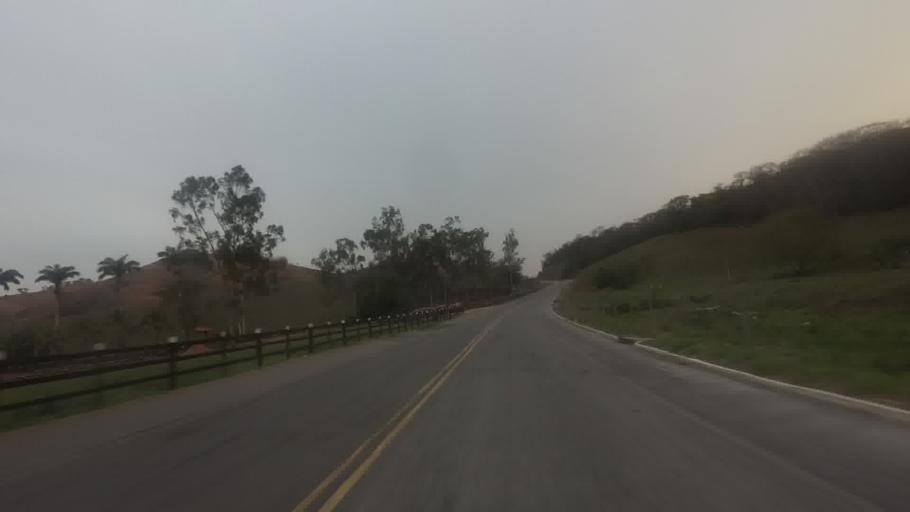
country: BR
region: Minas Gerais
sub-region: Recreio
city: Recreio
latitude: -21.7082
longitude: -42.4242
